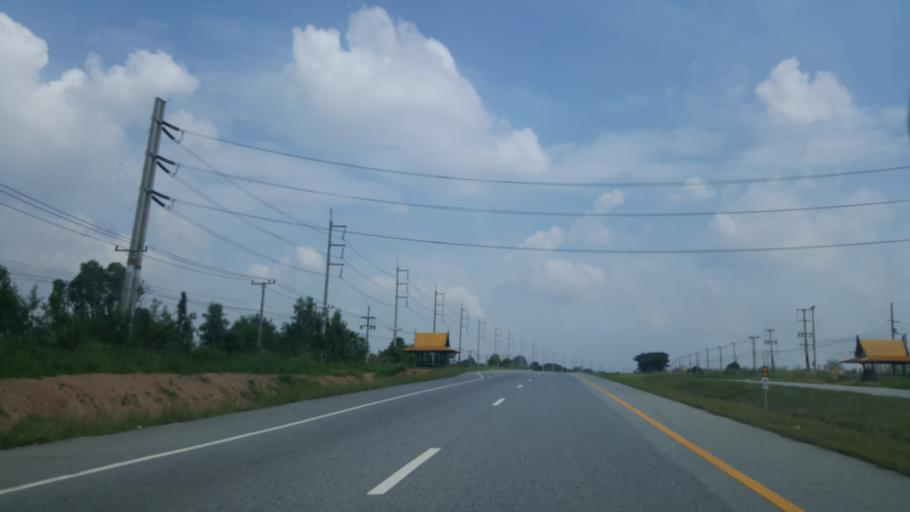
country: TH
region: Chon Buri
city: Phatthaya
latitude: 12.9167
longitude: 101.0305
